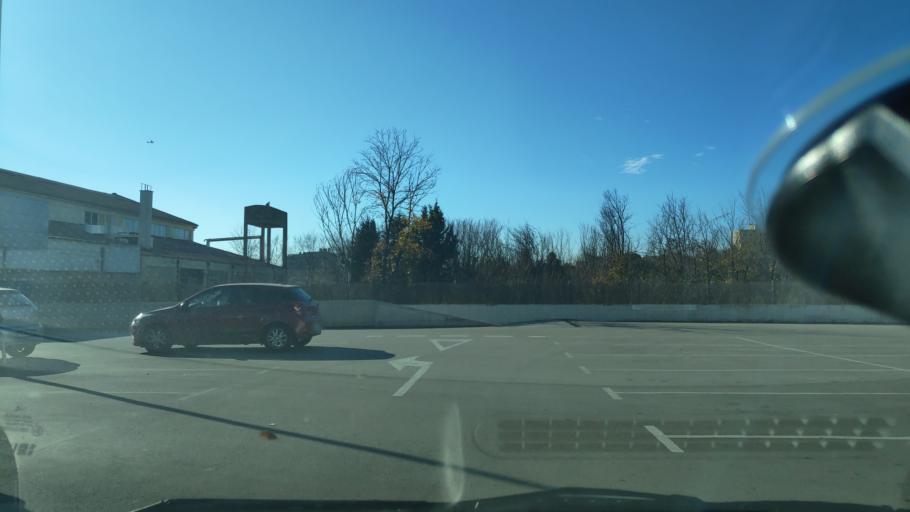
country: ES
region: Catalonia
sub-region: Provincia de Barcelona
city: Sant Quirze del Valles
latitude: 41.5422
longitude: 2.0932
